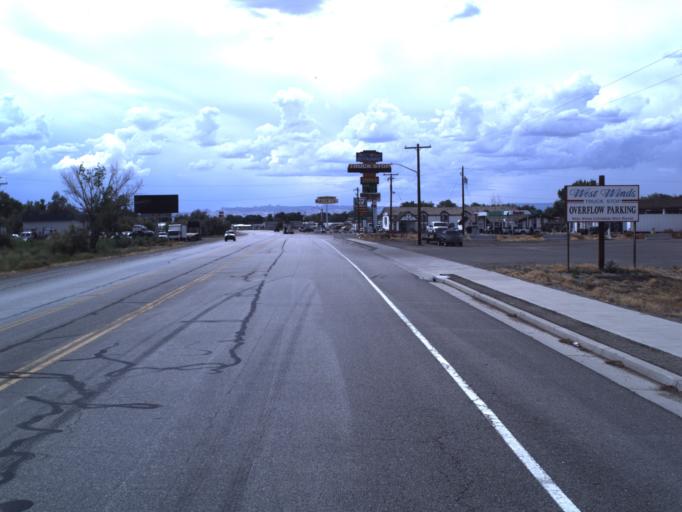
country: US
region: Utah
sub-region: Carbon County
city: East Carbon City
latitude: 38.9945
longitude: -110.1466
